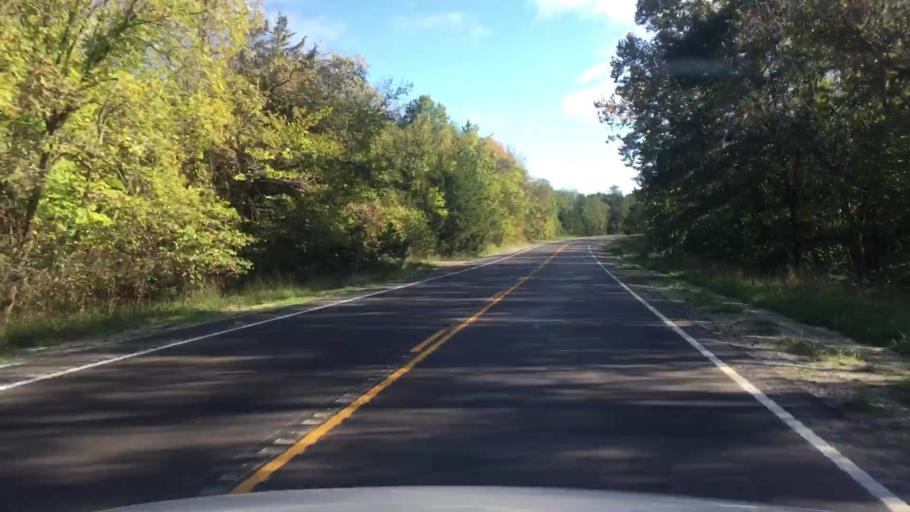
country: US
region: Missouri
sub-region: Howard County
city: New Franklin
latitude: 38.9878
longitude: -92.5358
